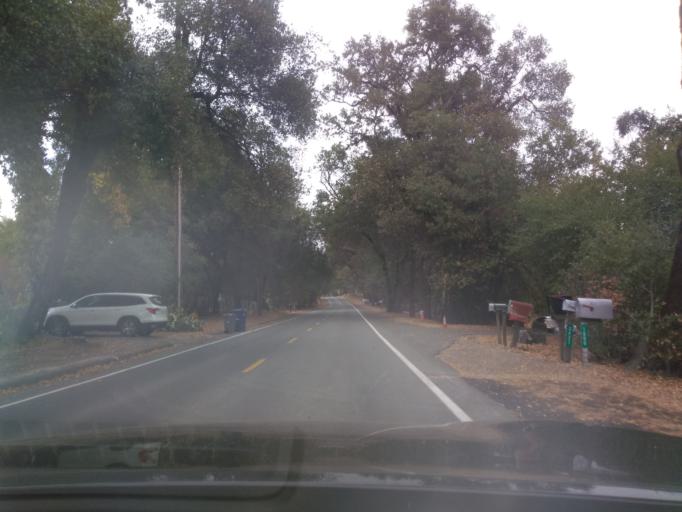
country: US
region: California
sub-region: Mendocino County
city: Ukiah
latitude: 39.1975
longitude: -123.1897
